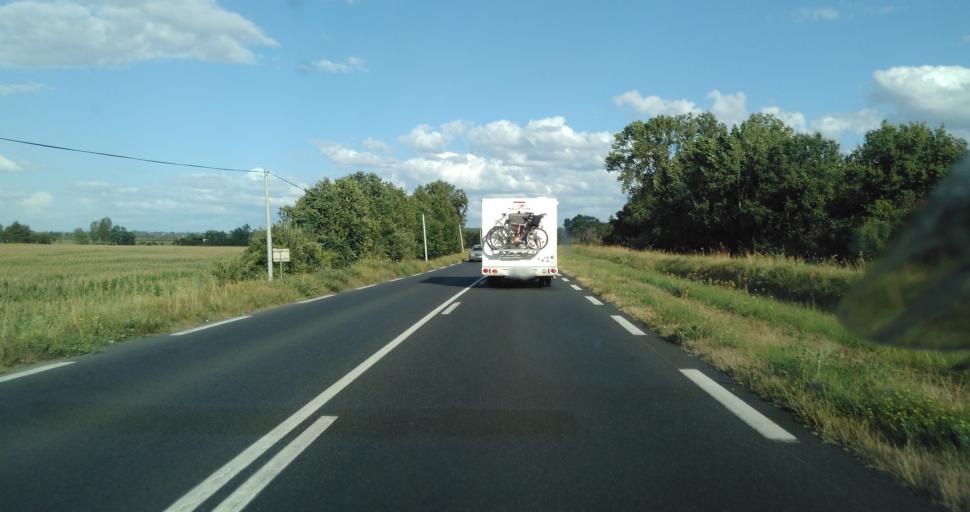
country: FR
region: Centre
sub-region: Departement d'Indre-et-Loire
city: Noizay
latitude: 47.4039
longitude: 0.9032
